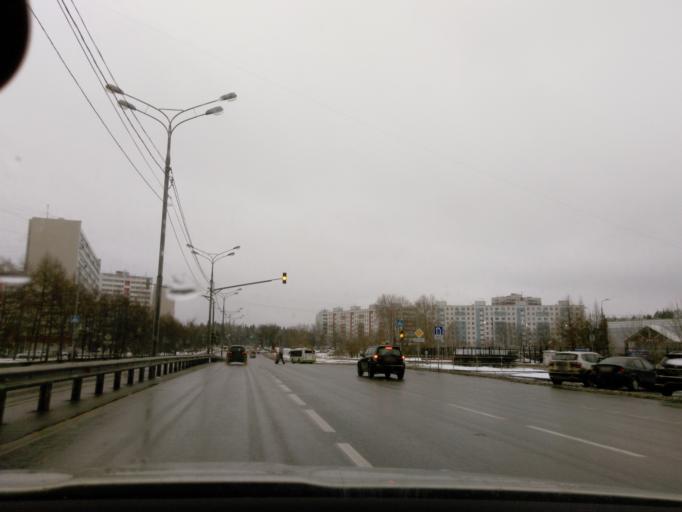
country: RU
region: Moskovskaya
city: Rzhavki
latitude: 55.9888
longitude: 37.2256
